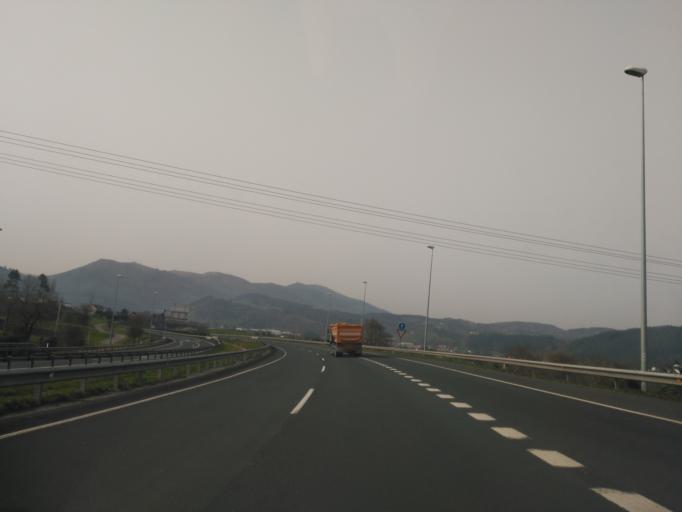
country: ES
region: Cantabria
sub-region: Provincia de Cantabria
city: Torrelavega
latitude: 43.3292
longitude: -4.0480
